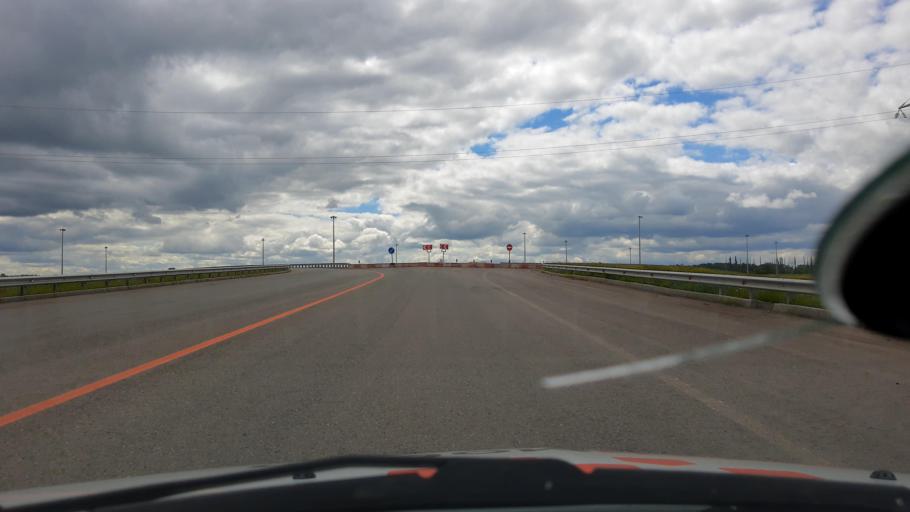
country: RU
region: Bashkortostan
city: Buzdyak
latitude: 54.6477
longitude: 54.5381
